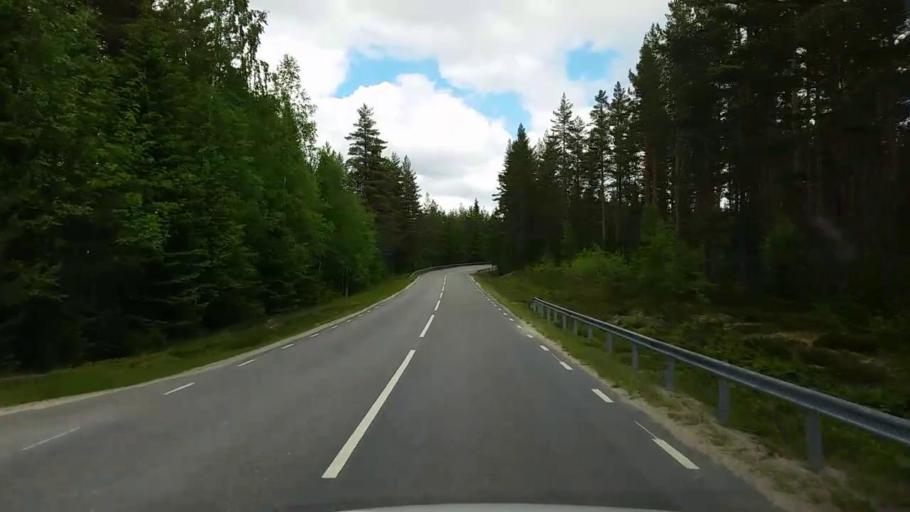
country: SE
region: Gaevleborg
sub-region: Bollnas Kommun
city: Vittsjo
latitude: 61.1170
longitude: 16.1486
